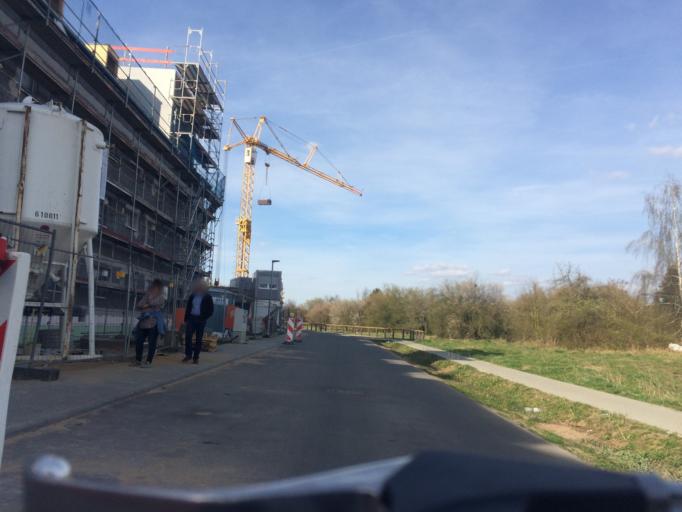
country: DE
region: Hesse
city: Morfelden-Walldorf
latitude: 49.9811
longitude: 8.5658
